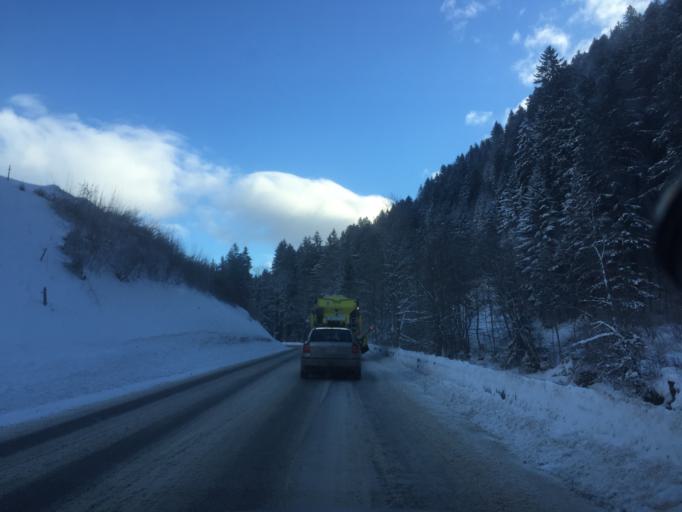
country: FR
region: Rhone-Alpes
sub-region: Departement de la Haute-Savoie
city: Abondance
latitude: 46.2818
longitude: 6.7303
